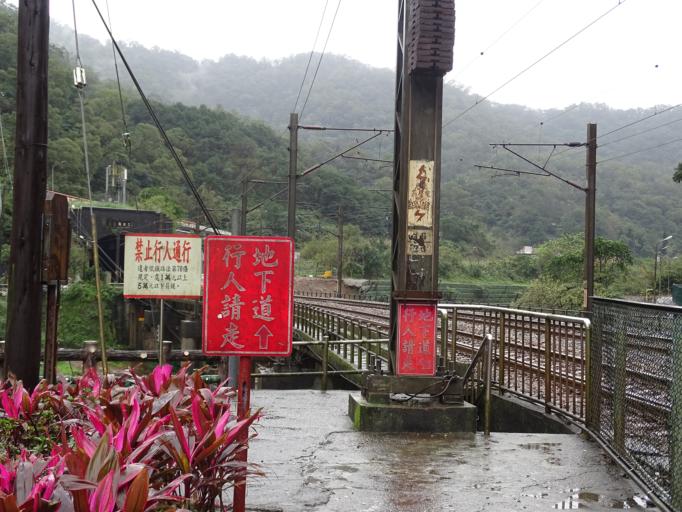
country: TW
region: Taiwan
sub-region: Keelung
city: Keelung
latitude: 25.0629
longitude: 121.8227
